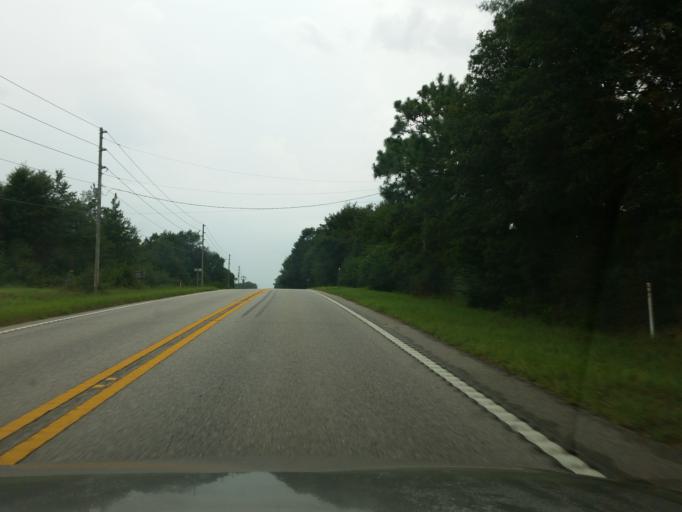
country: US
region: Alabama
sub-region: Baldwin County
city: Elberta
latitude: 30.5348
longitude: -87.5282
